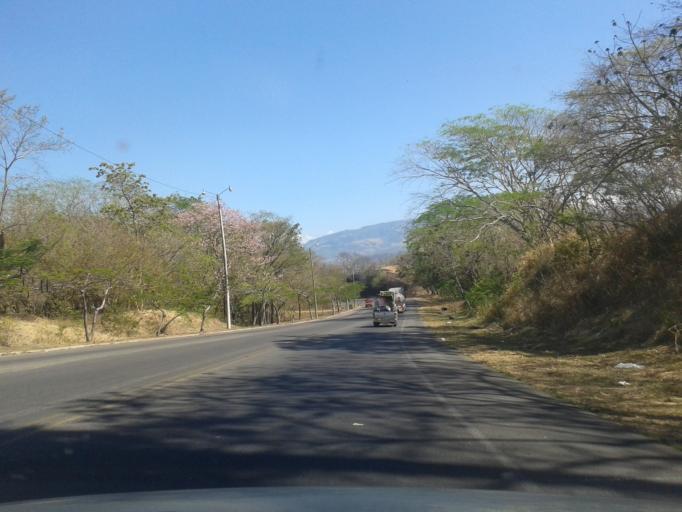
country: CR
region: Puntarenas
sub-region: Canton Central de Puntarenas
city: Chacarita
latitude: 9.9529
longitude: -84.7313
